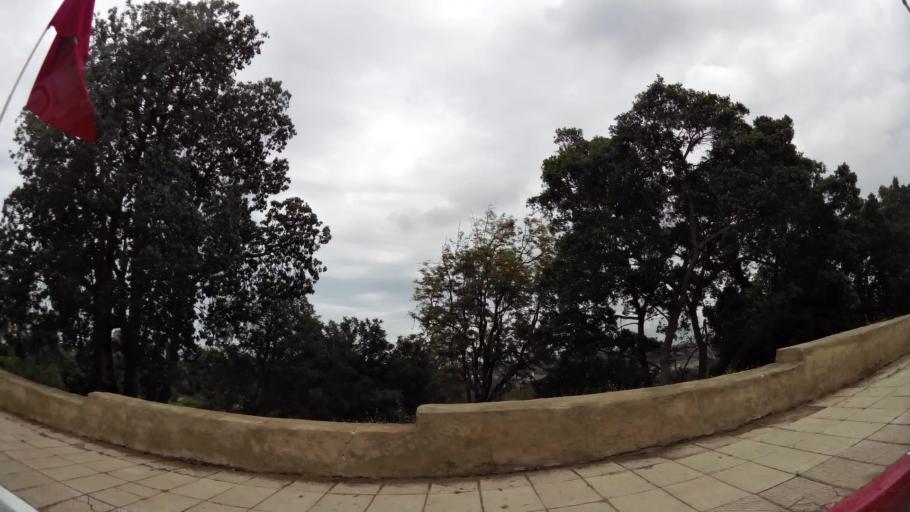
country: MA
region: Rabat-Sale-Zemmour-Zaer
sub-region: Rabat
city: Rabat
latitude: 34.0161
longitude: -6.8211
